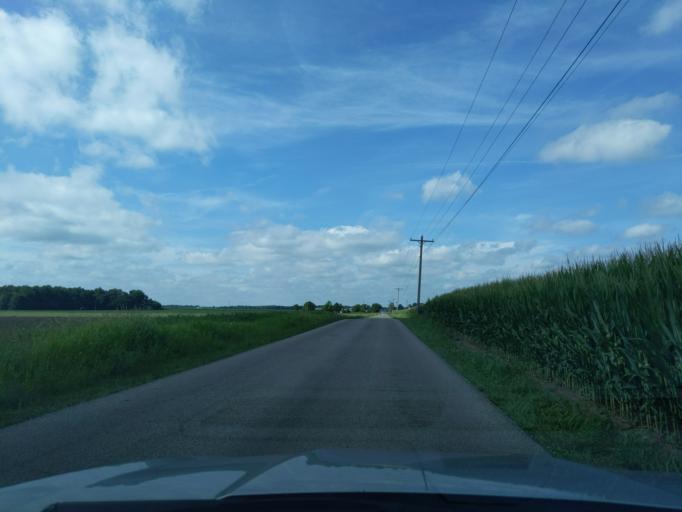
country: US
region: Indiana
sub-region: Ripley County
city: Batesville
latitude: 39.2900
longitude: -85.3477
